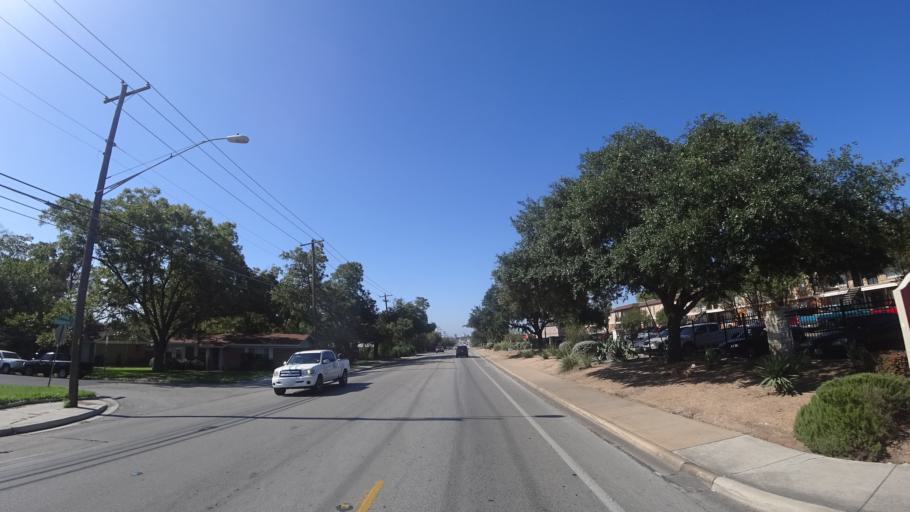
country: US
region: Texas
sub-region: Travis County
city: Austin
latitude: 30.3154
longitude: -97.7020
